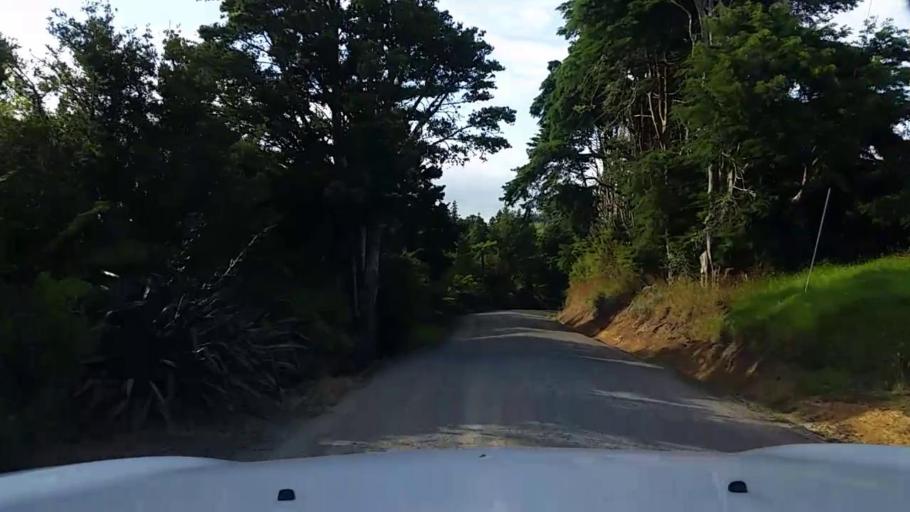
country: NZ
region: Northland
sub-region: Whangarei
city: Maungatapere
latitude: -35.6756
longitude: 174.1767
